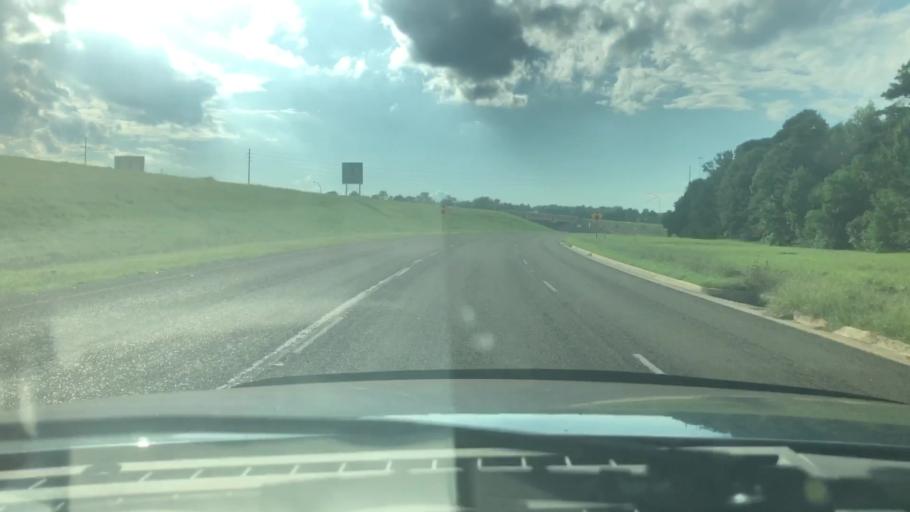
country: US
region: Texas
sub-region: Bowie County
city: Wake Village
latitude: 33.3865
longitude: -94.0886
